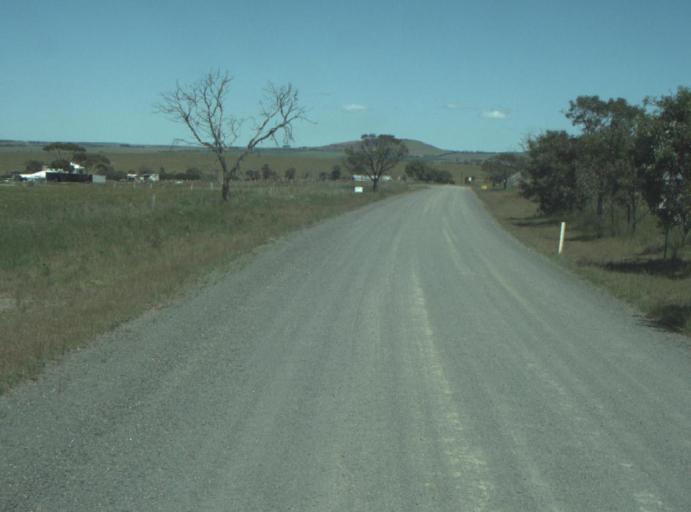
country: AU
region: Victoria
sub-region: Greater Geelong
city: Lara
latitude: -37.8923
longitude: 144.3790
